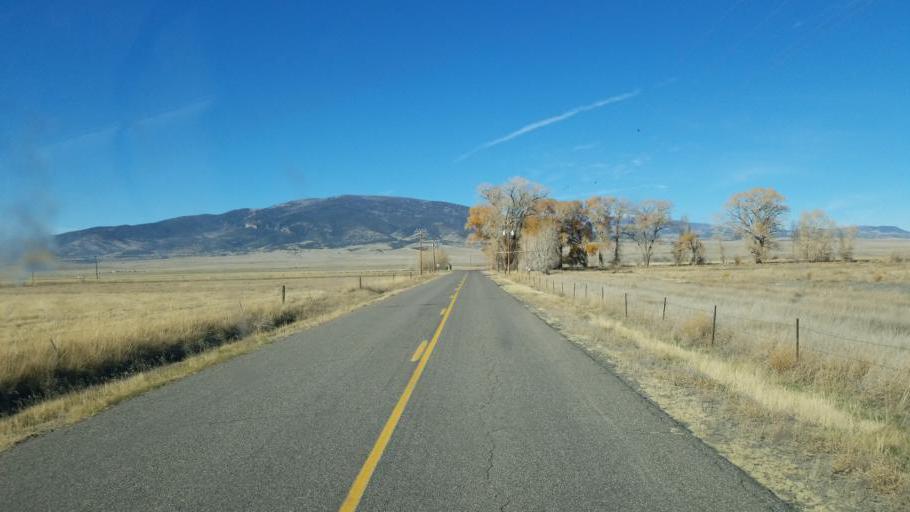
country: US
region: Colorado
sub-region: Rio Grande County
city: Monte Vista
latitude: 37.4587
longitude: -106.1459
